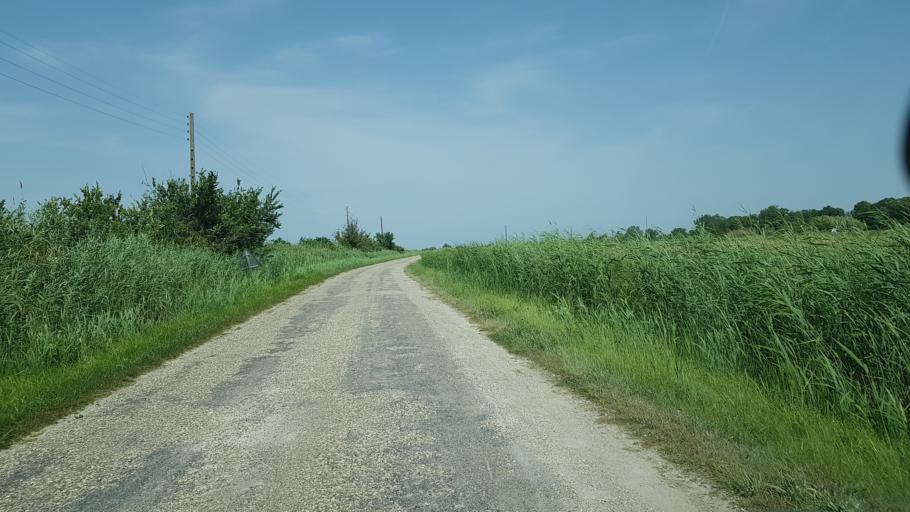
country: FR
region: Provence-Alpes-Cote d'Azur
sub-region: Departement des Bouches-du-Rhone
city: Arles
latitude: 43.5072
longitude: 4.6350
